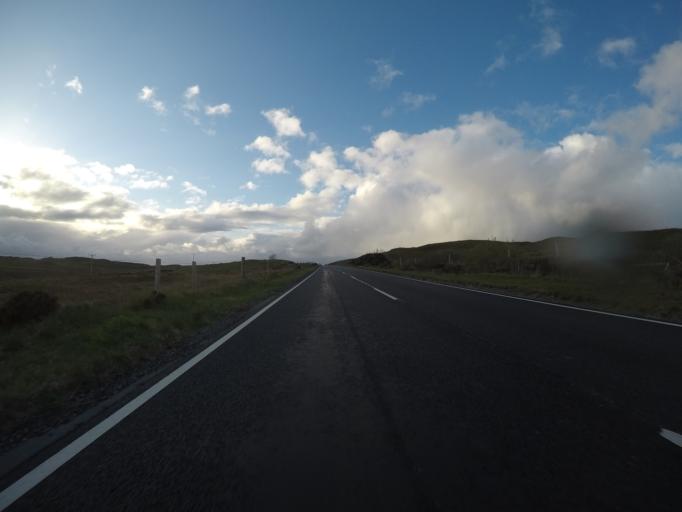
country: GB
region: Scotland
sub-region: Highland
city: Portree
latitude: 57.5376
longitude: -6.3620
